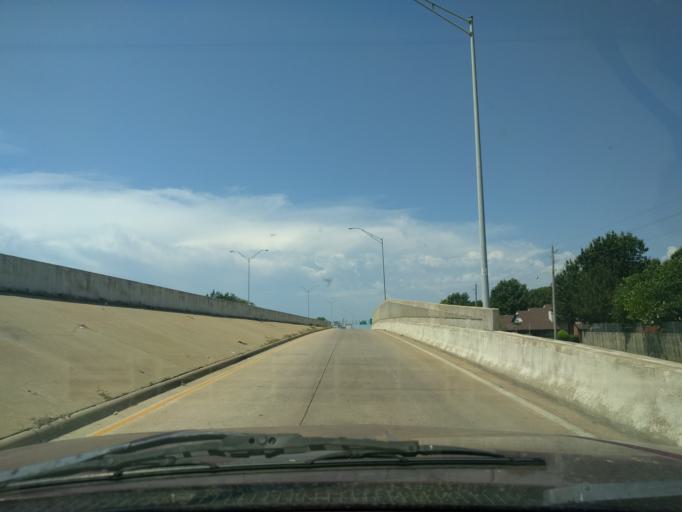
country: US
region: Oklahoma
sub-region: Tulsa County
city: Broken Arrow
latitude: 36.1451
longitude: -95.8524
